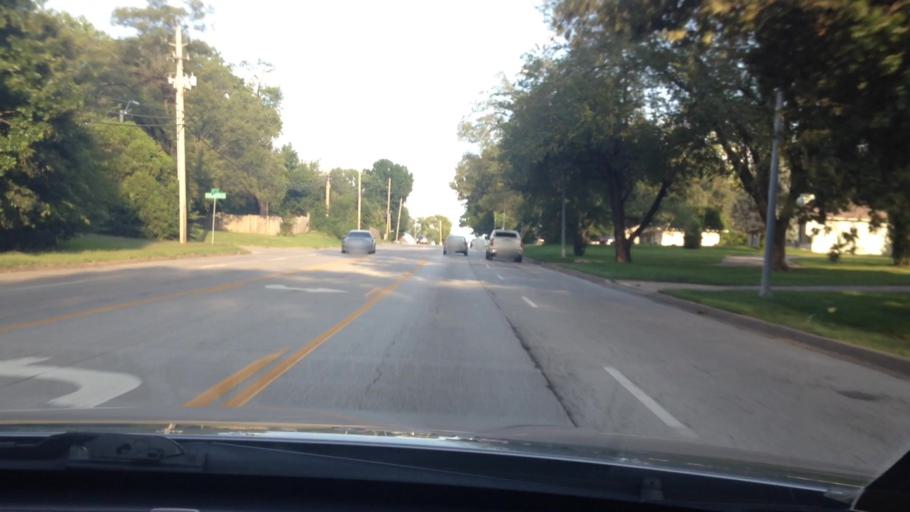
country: US
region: Missouri
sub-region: Jackson County
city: Raytown
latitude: 38.9668
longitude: -94.5063
